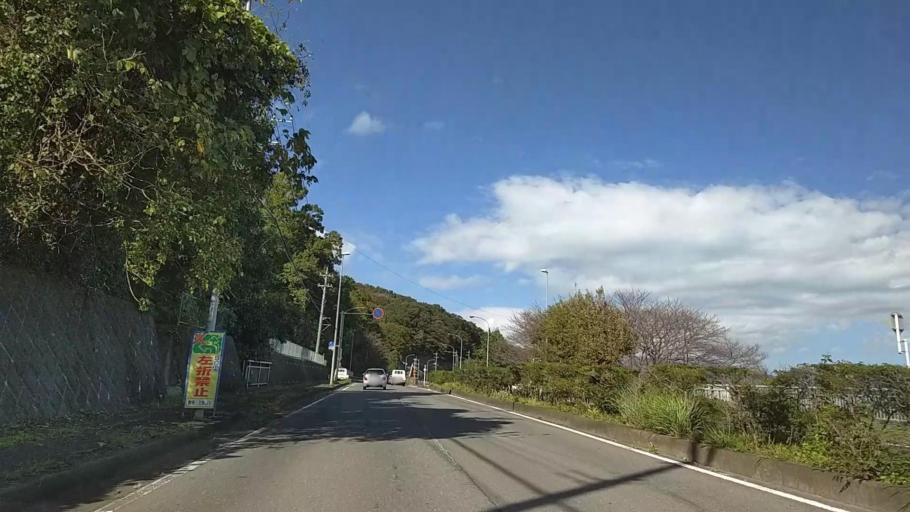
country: JP
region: Kanagawa
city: Ninomiya
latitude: 35.3268
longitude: 139.2344
